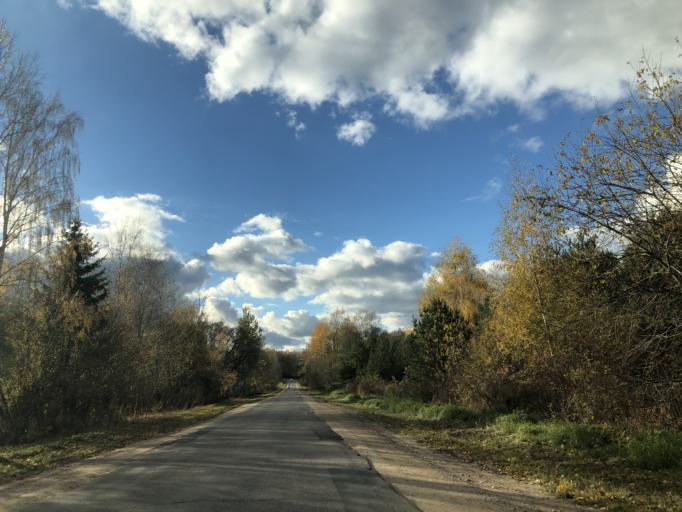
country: LT
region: Utenos apskritis
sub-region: Anyksciai
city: Anyksciai
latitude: 55.5167
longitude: 25.1298
